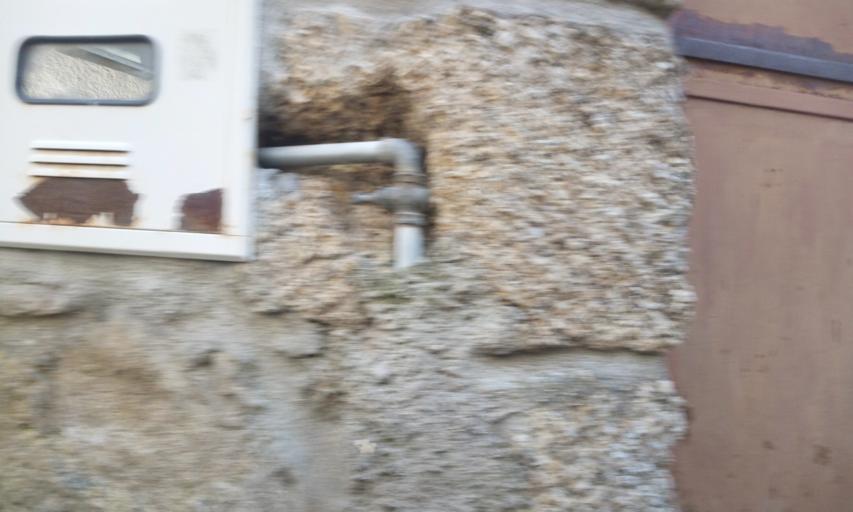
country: PT
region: Guarda
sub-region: Seia
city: Seia
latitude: 40.4660
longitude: -7.6225
